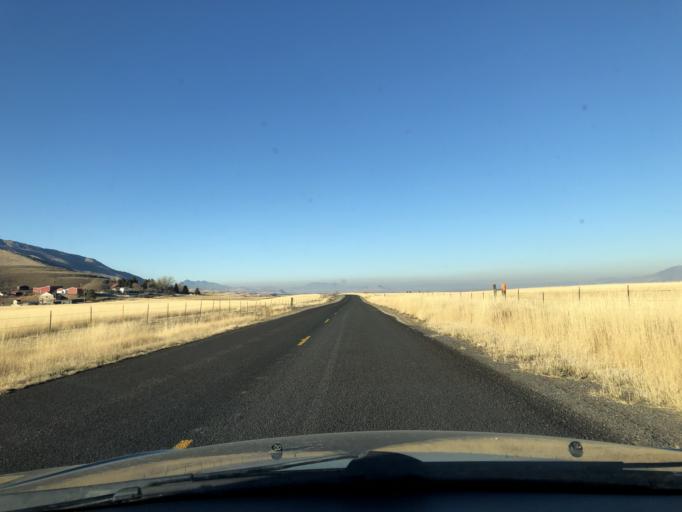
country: US
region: Utah
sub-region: Cache County
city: Wellsville
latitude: 41.5894
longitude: -111.9265
